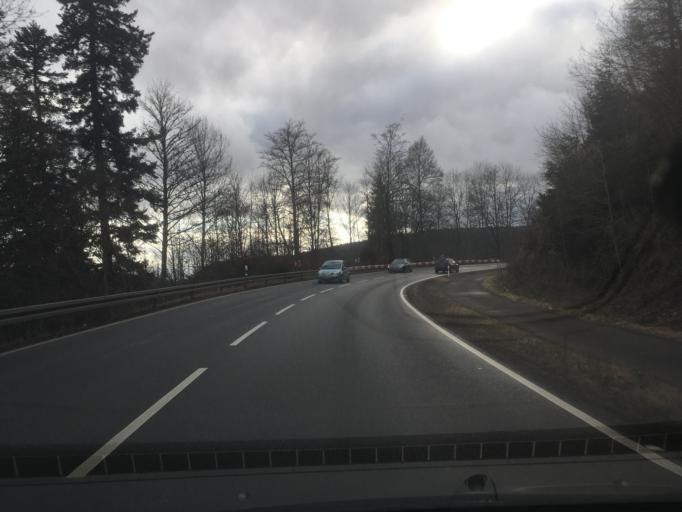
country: DE
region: Baden-Wuerttemberg
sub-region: Freiburg Region
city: Hausern
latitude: 47.7589
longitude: 8.1858
